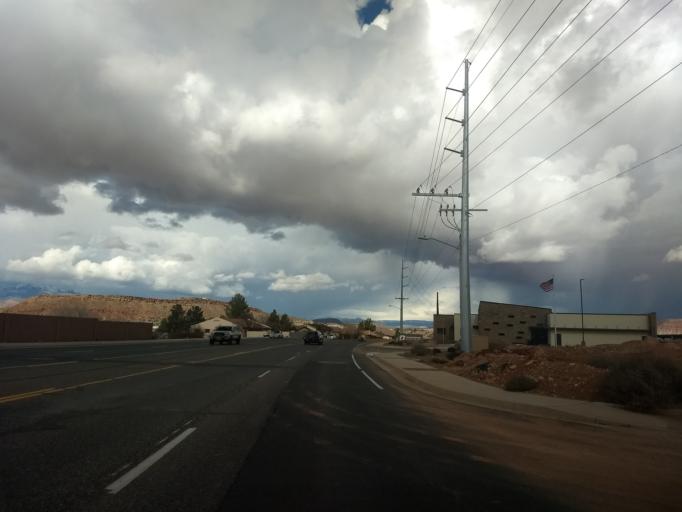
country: US
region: Utah
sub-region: Washington County
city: Saint George
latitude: 37.0562
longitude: -113.5514
